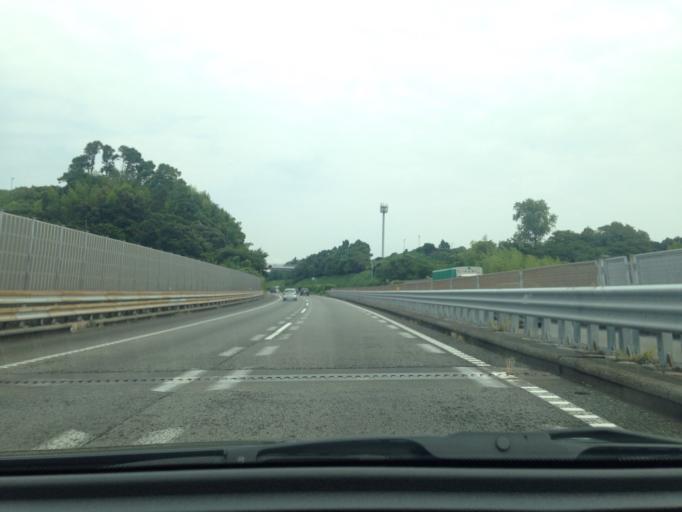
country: JP
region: Shizuoka
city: Shimada
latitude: 34.7761
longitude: 138.2282
